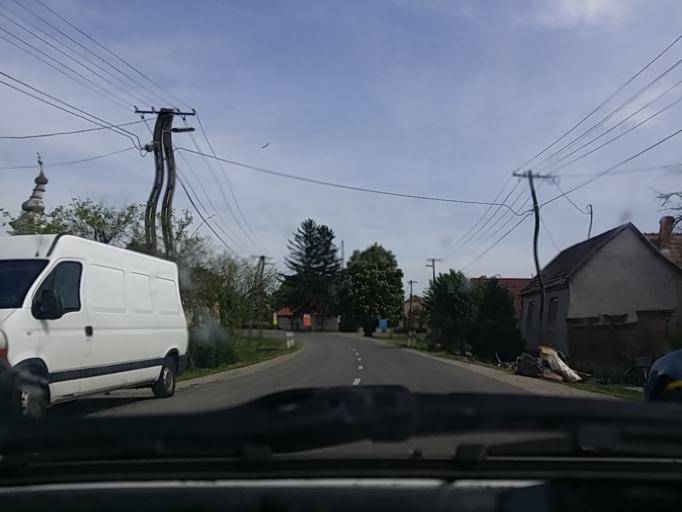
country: HR
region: Osjecko-Baranjska
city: Viljevo
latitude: 45.8250
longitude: 18.0997
